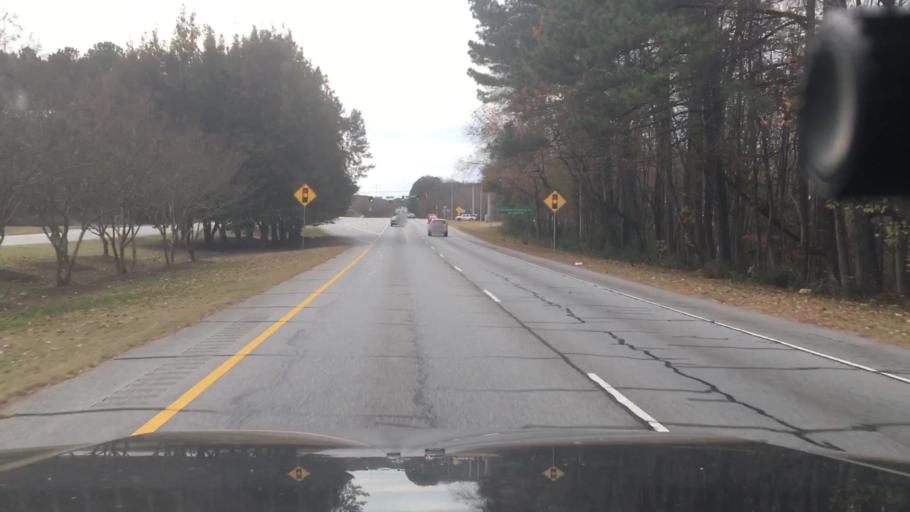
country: US
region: Georgia
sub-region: Coweta County
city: Newnan
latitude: 33.3895
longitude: -84.7742
